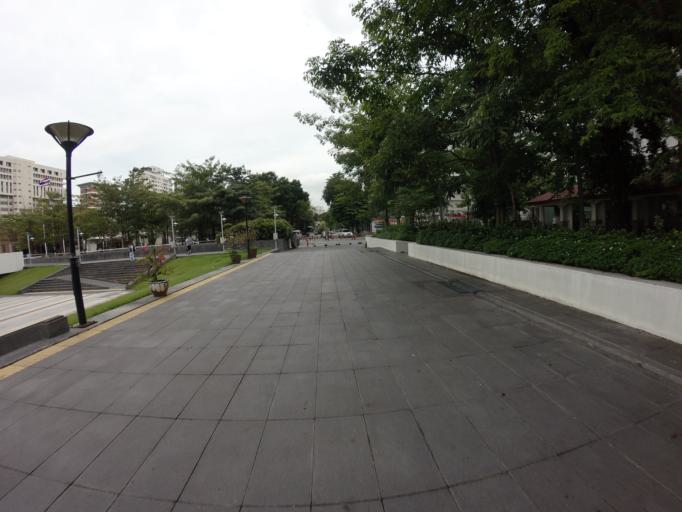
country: TH
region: Bangkok
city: Watthana
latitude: 13.7440
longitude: 100.5646
